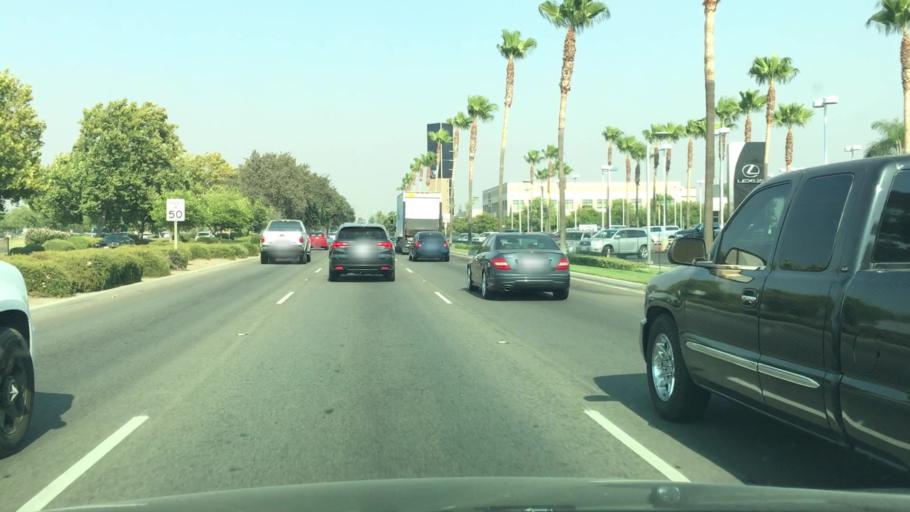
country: US
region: California
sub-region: Fresno County
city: Fresno
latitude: 36.8369
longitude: -119.8070
